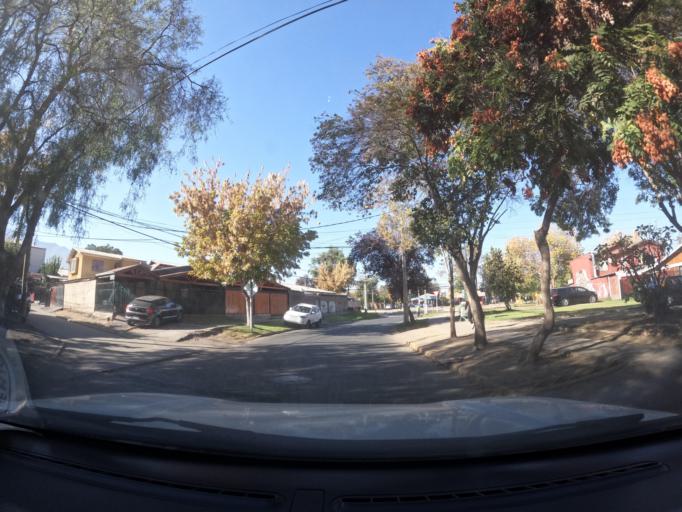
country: CL
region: Santiago Metropolitan
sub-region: Provincia de Santiago
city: Villa Presidente Frei, Nunoa, Santiago, Chile
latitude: -33.5013
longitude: -70.5784
